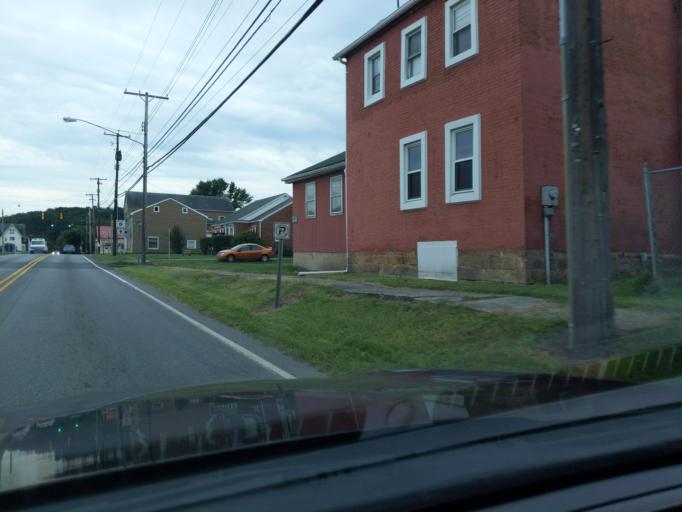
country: US
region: Pennsylvania
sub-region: Blair County
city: Duncansville
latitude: 40.3947
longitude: -78.4360
